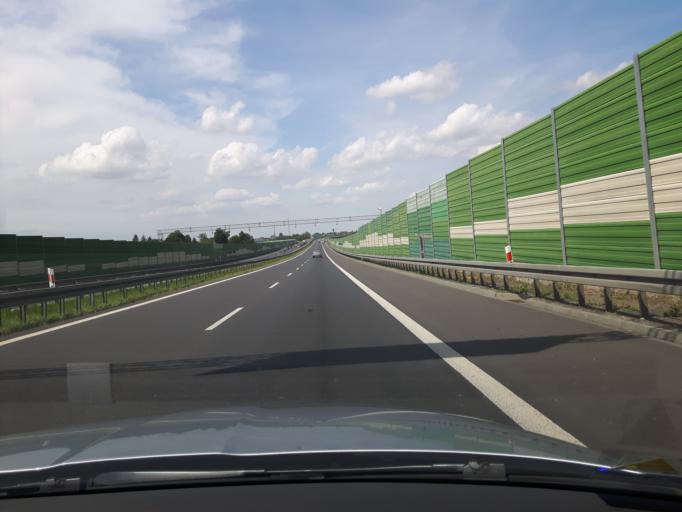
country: PL
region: Masovian Voivodeship
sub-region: Powiat plonski
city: Plonsk
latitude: 52.6074
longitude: 20.3974
